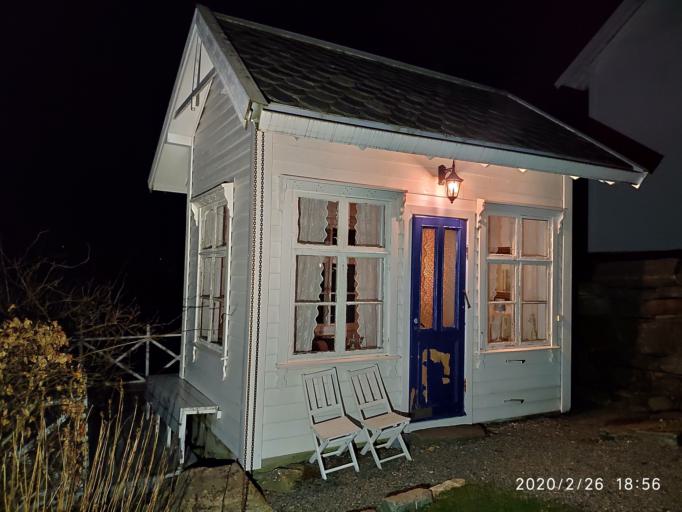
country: NO
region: Hordaland
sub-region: Tysnes
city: Uggdal
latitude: 60.0168
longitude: 5.5351
